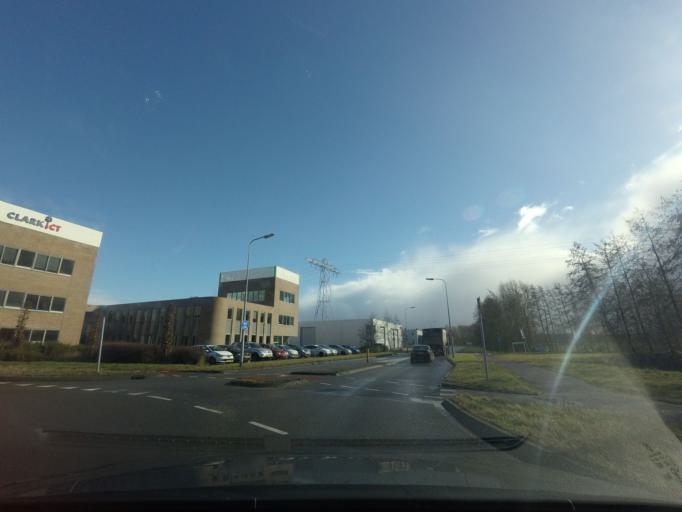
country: NL
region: Groningen
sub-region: Gemeente Groningen
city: Oosterpark
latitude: 53.2144
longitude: 6.6047
